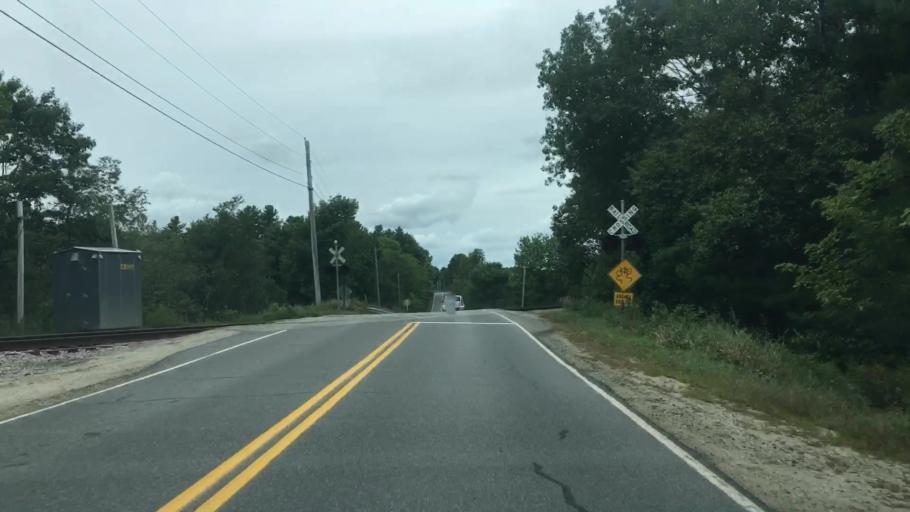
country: US
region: Maine
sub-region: Cumberland County
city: Yarmouth
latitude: 43.8599
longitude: -70.2190
